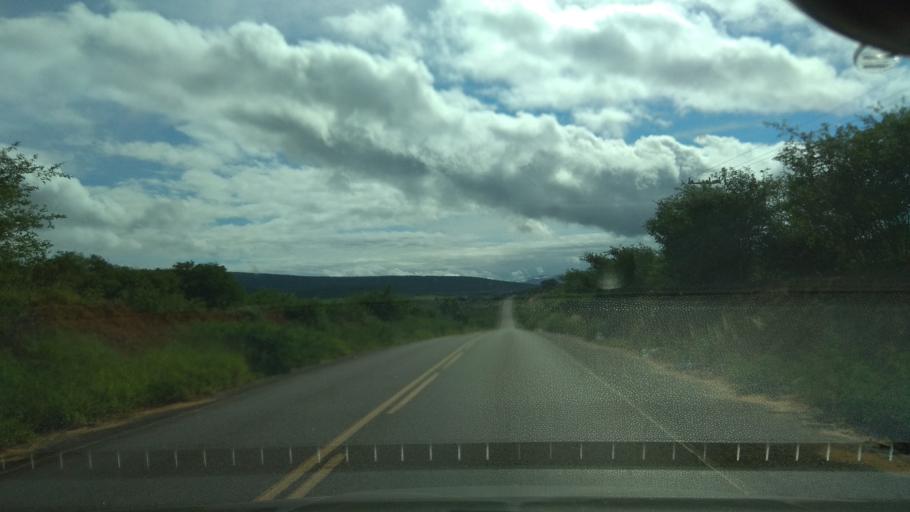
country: BR
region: Bahia
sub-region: Jaguaquara
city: Jaguaquara
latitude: -13.4391
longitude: -39.9318
